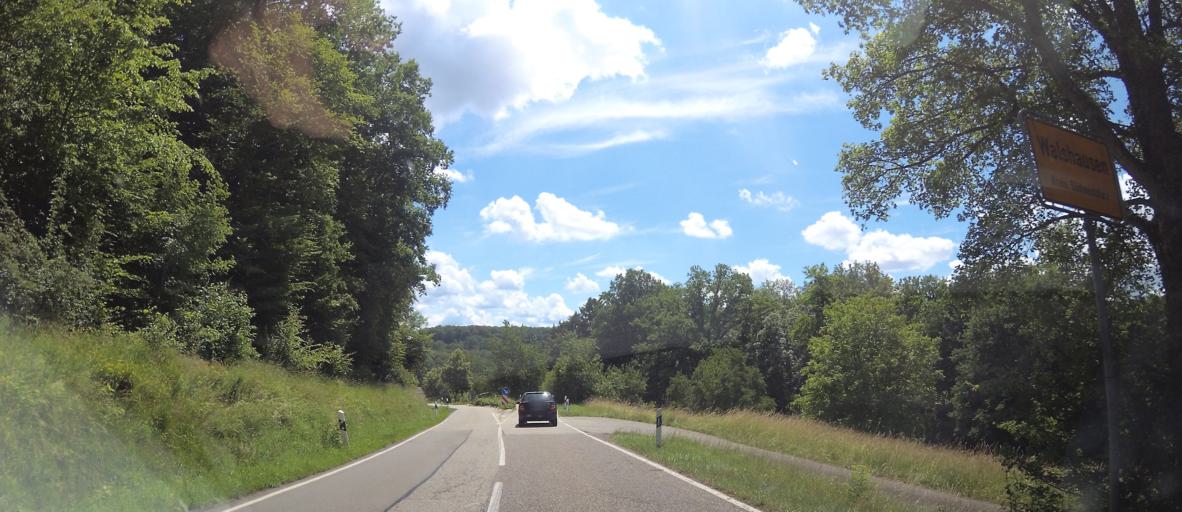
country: DE
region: Rheinland-Pfalz
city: Walshausen
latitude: 49.2143
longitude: 7.4751
